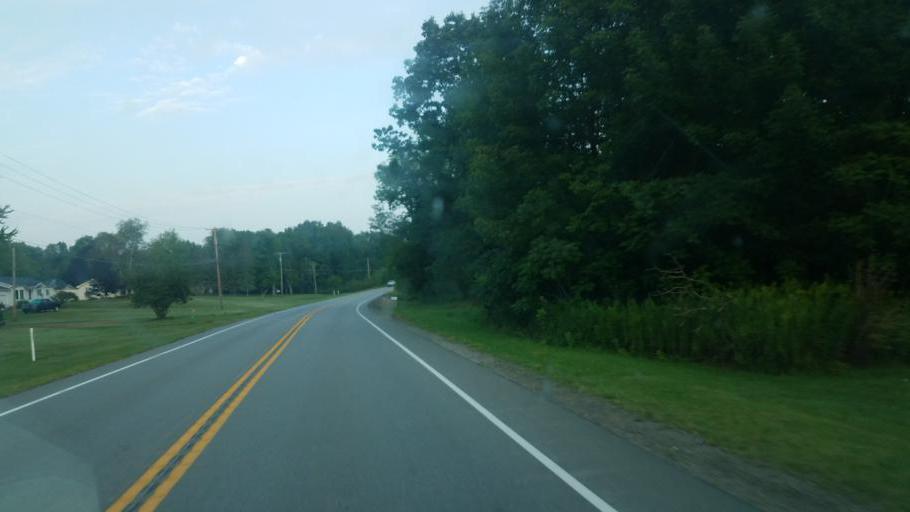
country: US
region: Pennsylvania
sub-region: Crawford County
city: Conneaut Lakeshore
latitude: 41.6036
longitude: -80.3283
